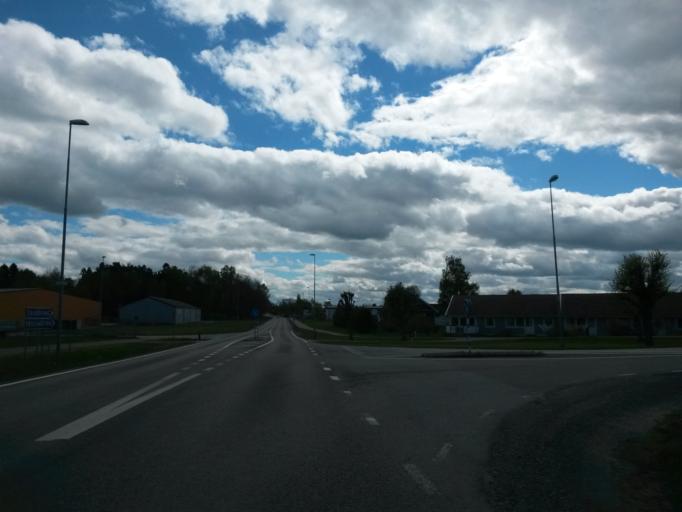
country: SE
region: Vaestra Goetaland
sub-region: Grastorps Kommun
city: Graestorp
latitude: 58.3401
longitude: 12.6870
